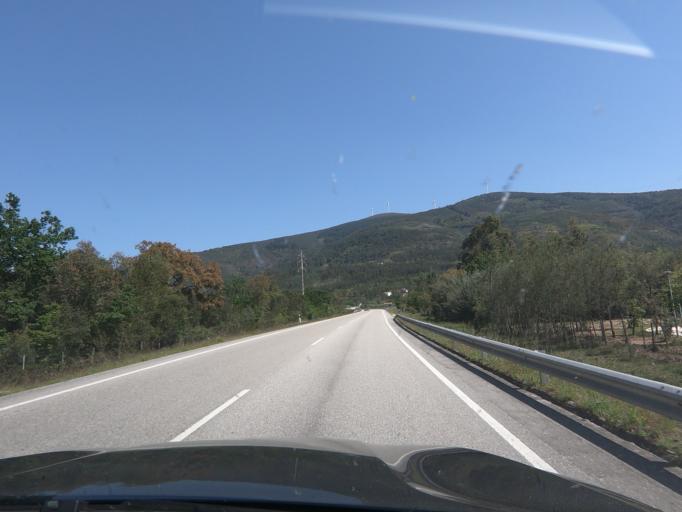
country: PT
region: Coimbra
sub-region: Lousa
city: Lousa
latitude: 40.1250
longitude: -8.2332
